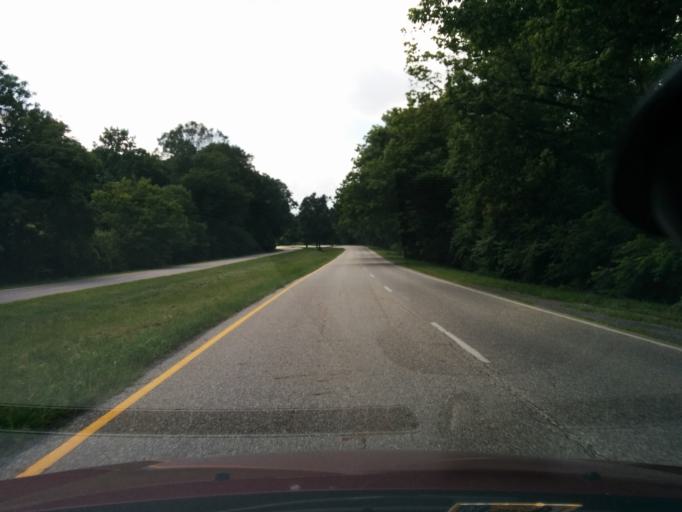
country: US
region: Virginia
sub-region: Rockbridge County
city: East Lexington
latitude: 37.8489
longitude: -79.3429
